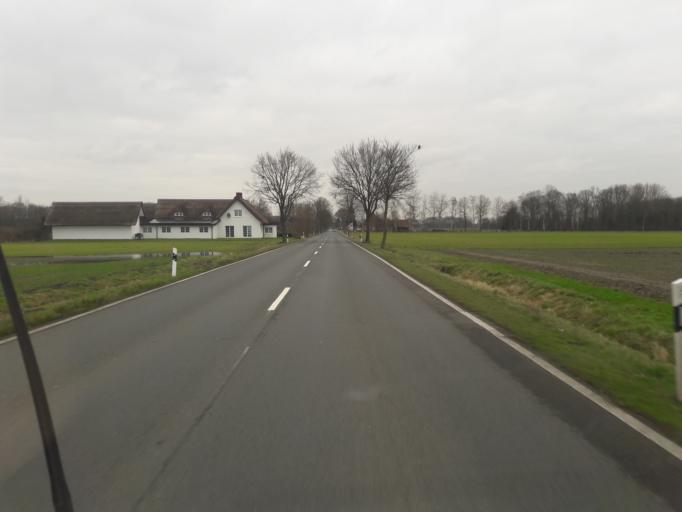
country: DE
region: Lower Saxony
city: Warmsen
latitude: 52.3887
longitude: 8.8527
